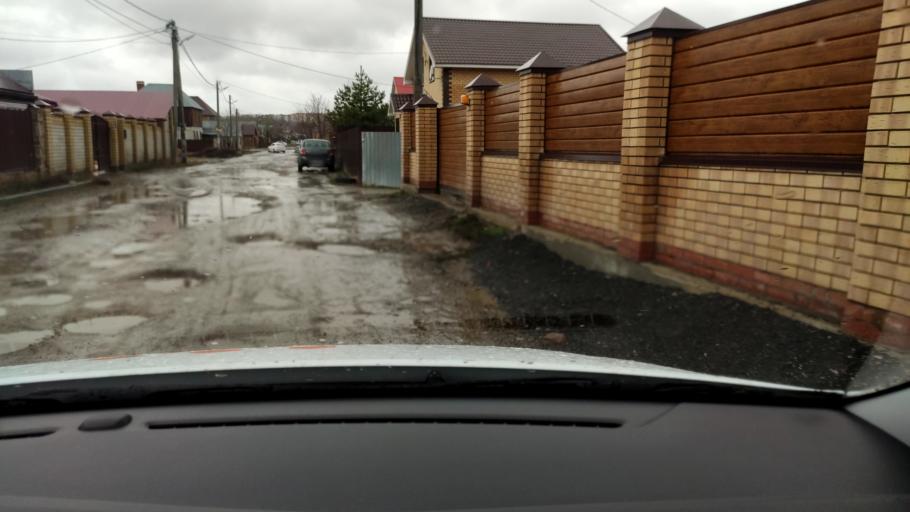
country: RU
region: Tatarstan
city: Stolbishchi
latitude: 55.7458
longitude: 49.2721
